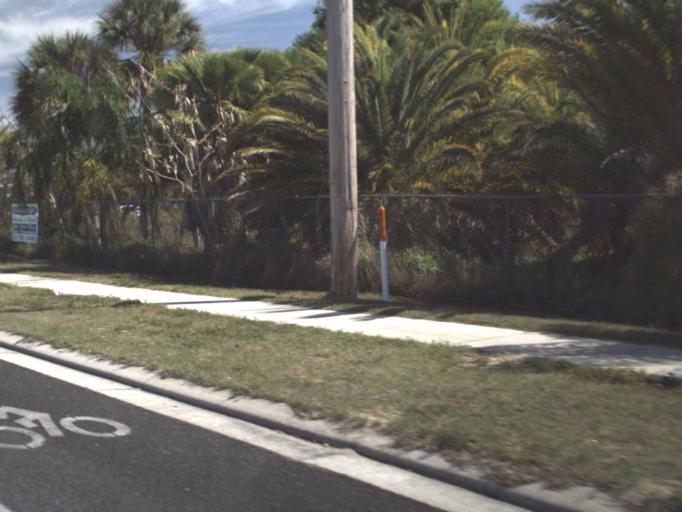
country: US
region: Florida
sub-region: Lake County
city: Fruitland Park
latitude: 28.8829
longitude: -81.9063
